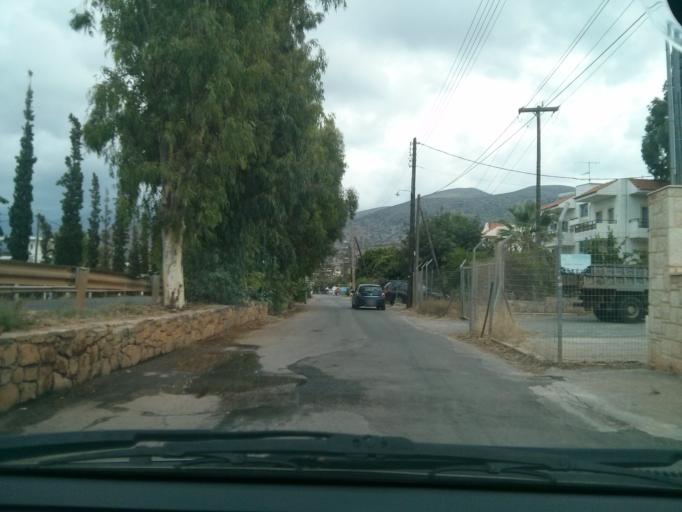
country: GR
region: Crete
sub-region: Nomos Irakleiou
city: Stalis
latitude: 35.2967
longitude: 25.4216
